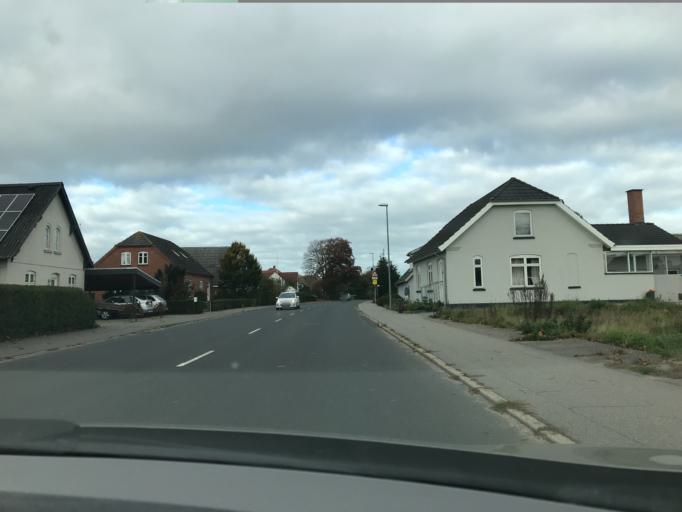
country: DK
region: South Denmark
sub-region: Kolding Kommune
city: Kolding
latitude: 55.5660
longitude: 9.4031
